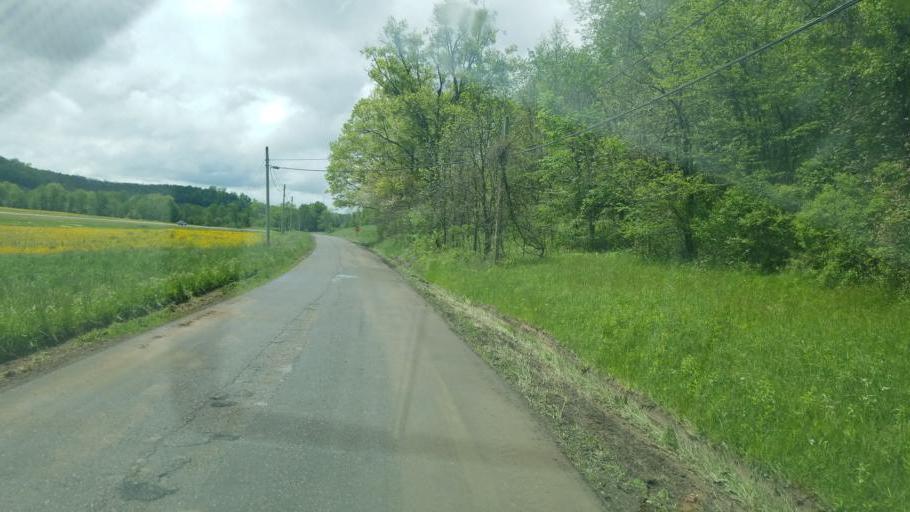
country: US
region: Ohio
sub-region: Tuscarawas County
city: Dennison
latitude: 40.3808
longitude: -81.2521
